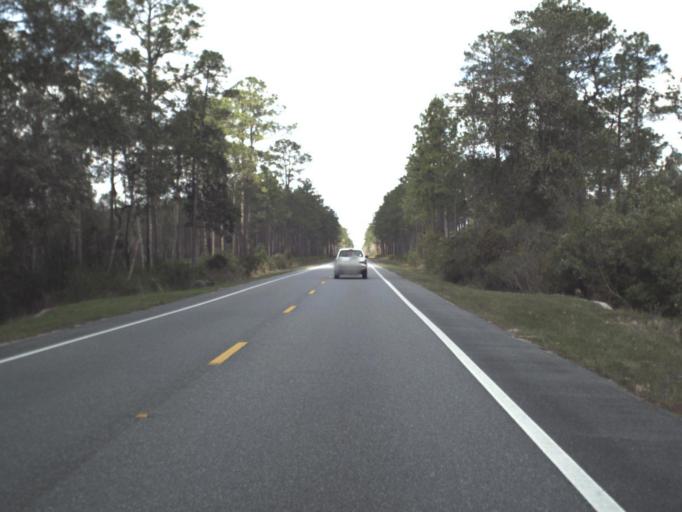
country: US
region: Florida
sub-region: Franklin County
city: Apalachicola
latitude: 29.9819
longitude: -84.9756
